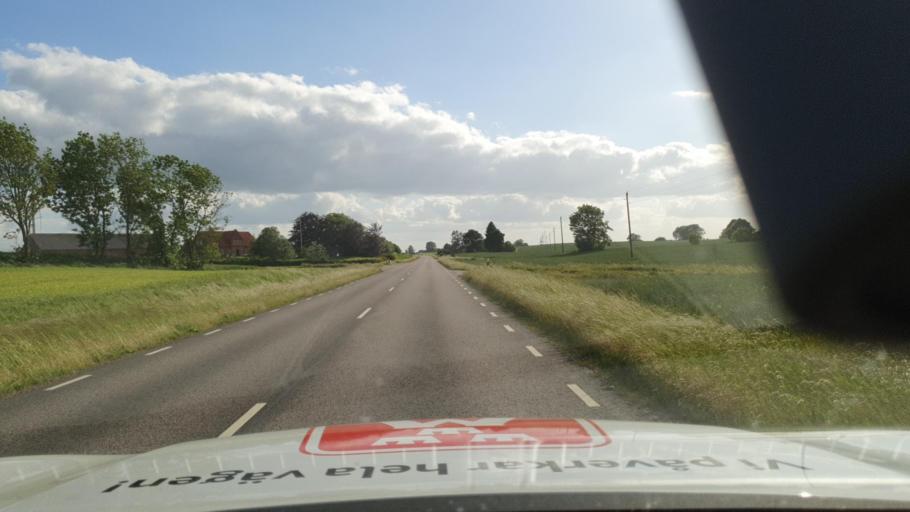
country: SE
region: Skane
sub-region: Tomelilla Kommun
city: Tomelilla
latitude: 55.5704
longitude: 13.9880
